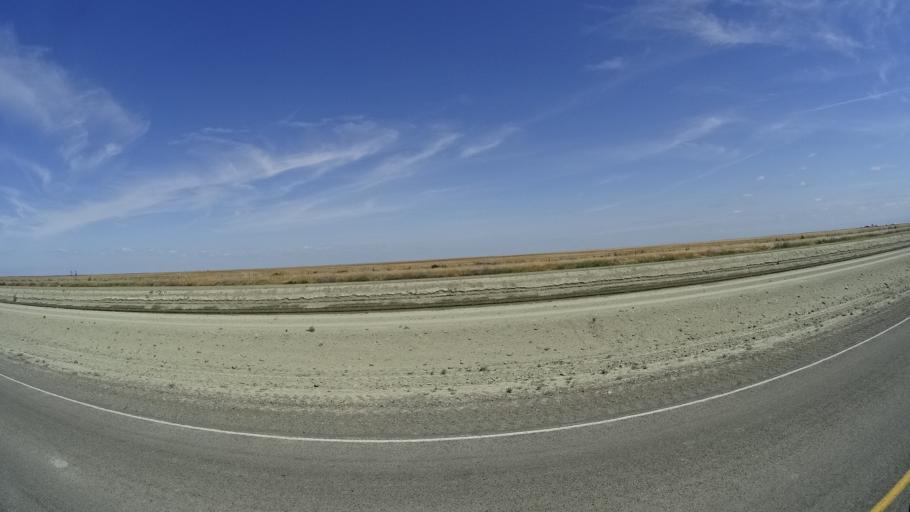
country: US
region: California
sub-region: Tulare County
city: Alpaugh
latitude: 35.9343
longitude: -119.6215
